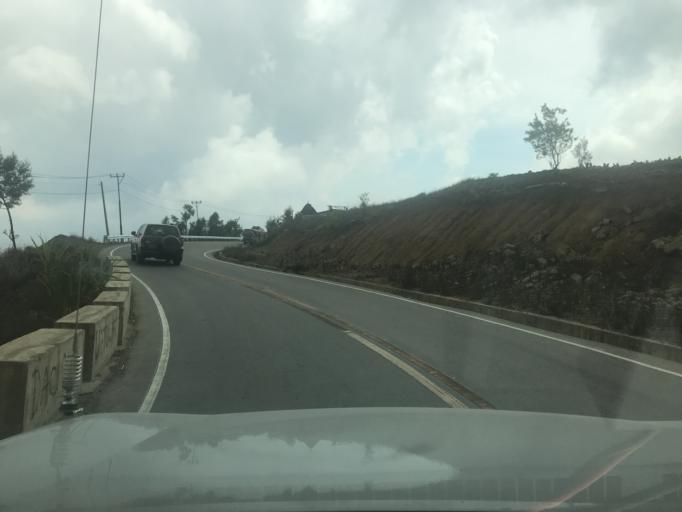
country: TL
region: Manufahi
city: Same
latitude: -8.8910
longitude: 125.5970
